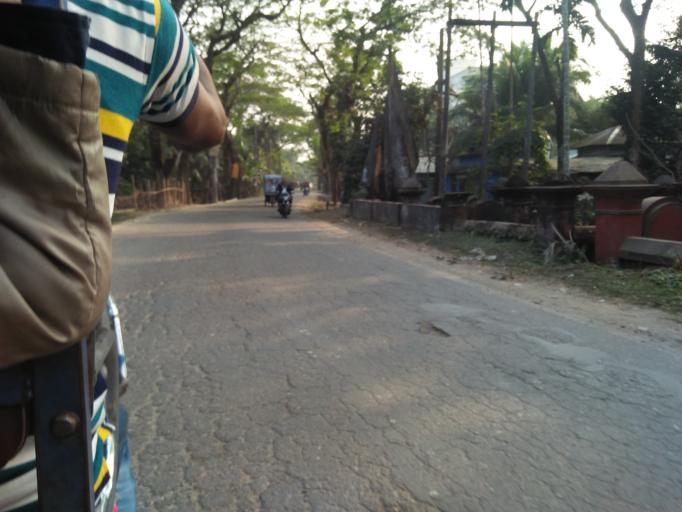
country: BD
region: Barisal
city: Bhola
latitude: 22.6966
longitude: 90.6435
